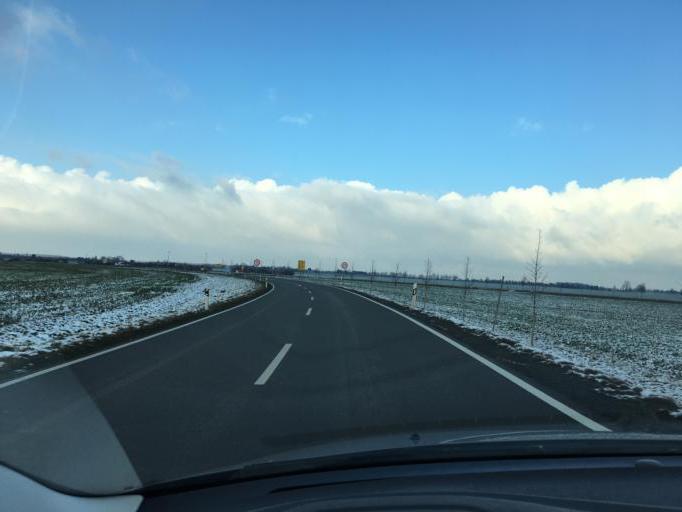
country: DE
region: Saxony
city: Brandis
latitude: 51.3416
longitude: 12.5968
